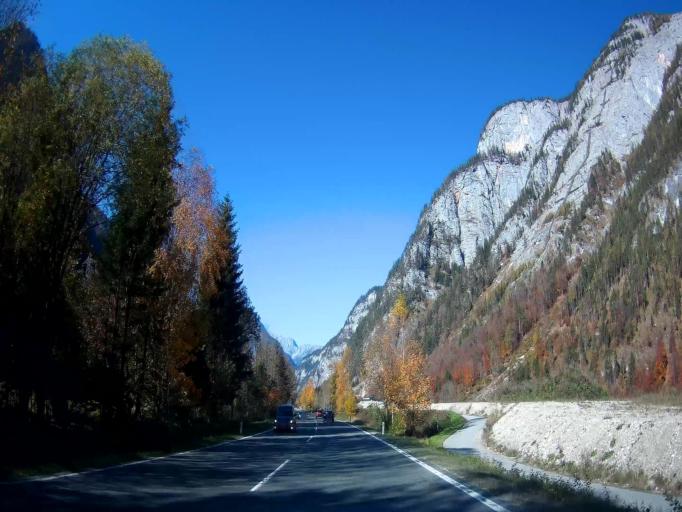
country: AT
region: Salzburg
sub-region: Politischer Bezirk Zell am See
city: Saalfelden am Steinernen Meer
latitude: 47.4885
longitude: 12.8232
